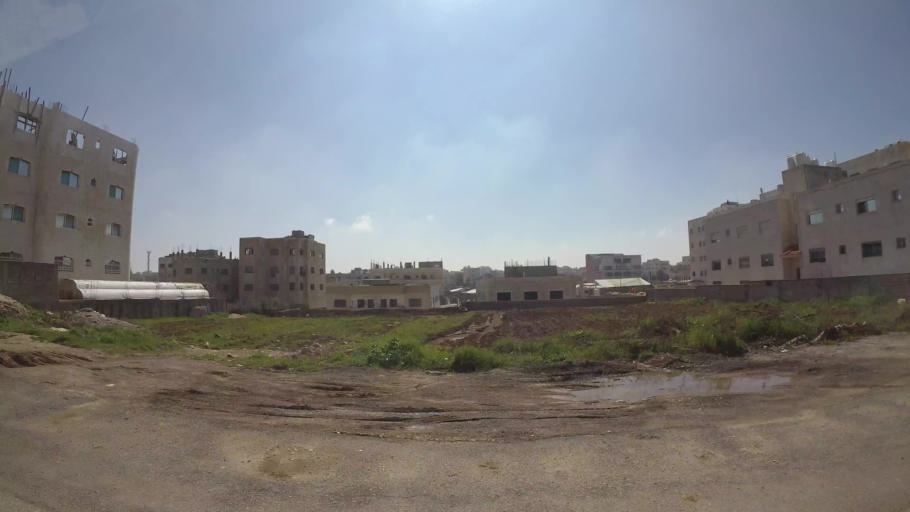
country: JO
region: Amman
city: Al Bunayyat ash Shamaliyah
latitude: 31.9006
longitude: 35.8977
